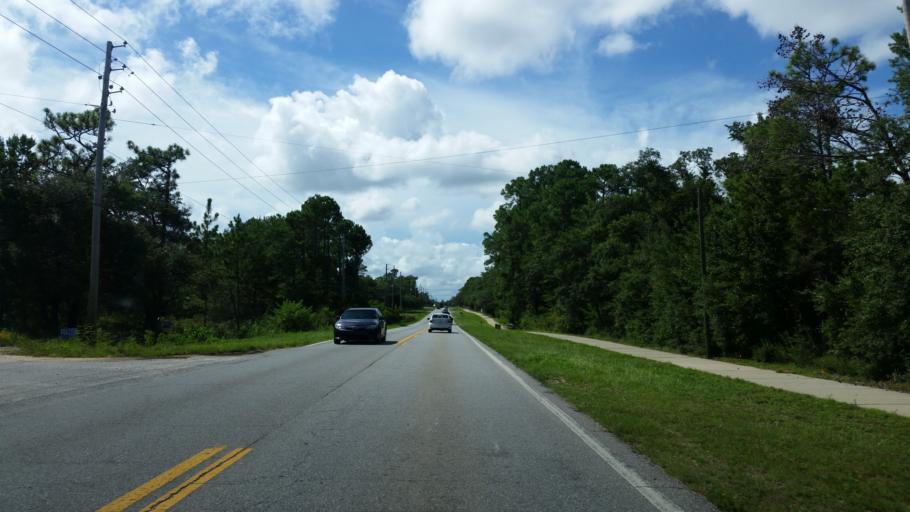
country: US
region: Florida
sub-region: Santa Rosa County
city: Holley
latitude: 30.4366
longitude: -86.9173
